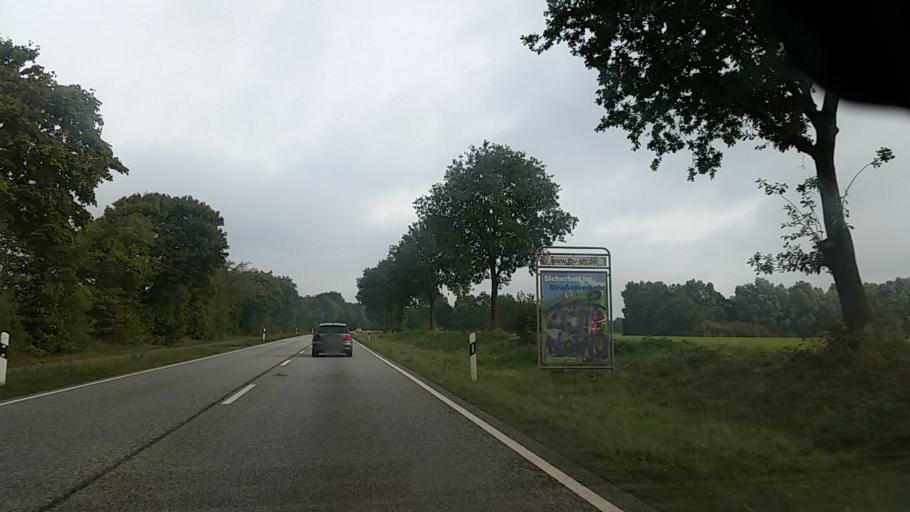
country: DE
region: Schleswig-Holstein
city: Norderstedt
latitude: 53.6948
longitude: 10.0089
